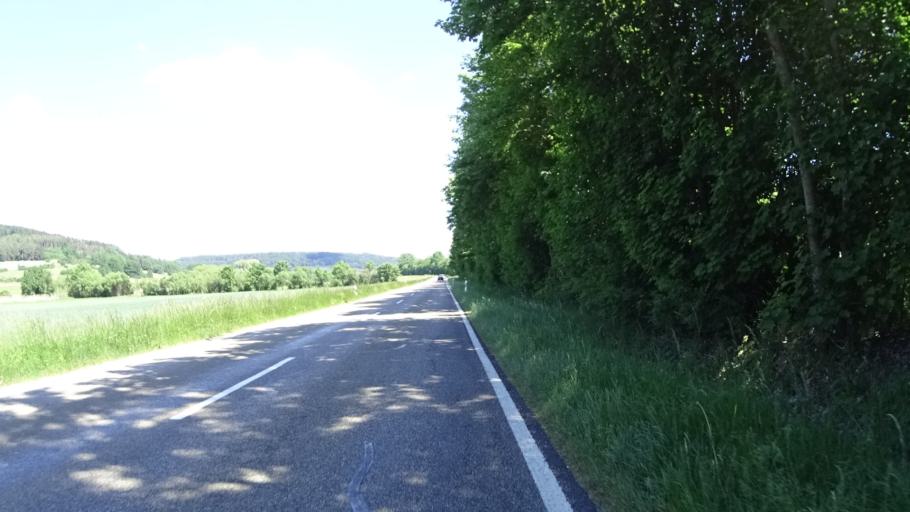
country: DE
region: Bavaria
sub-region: Regierungsbezirk Mittelfranken
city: Thalmassing
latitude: 49.0775
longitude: 11.2670
